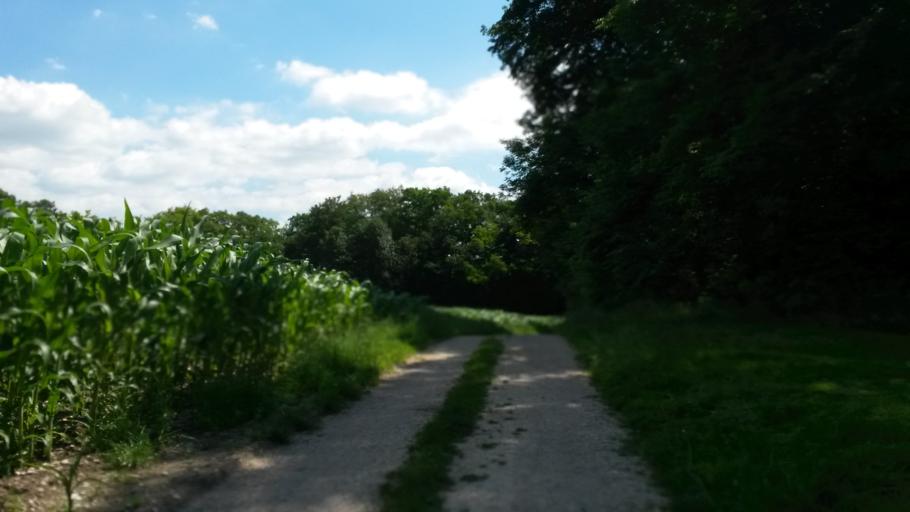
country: DE
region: Bavaria
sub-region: Upper Bavaria
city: Chieming
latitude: 47.9047
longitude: 12.5176
